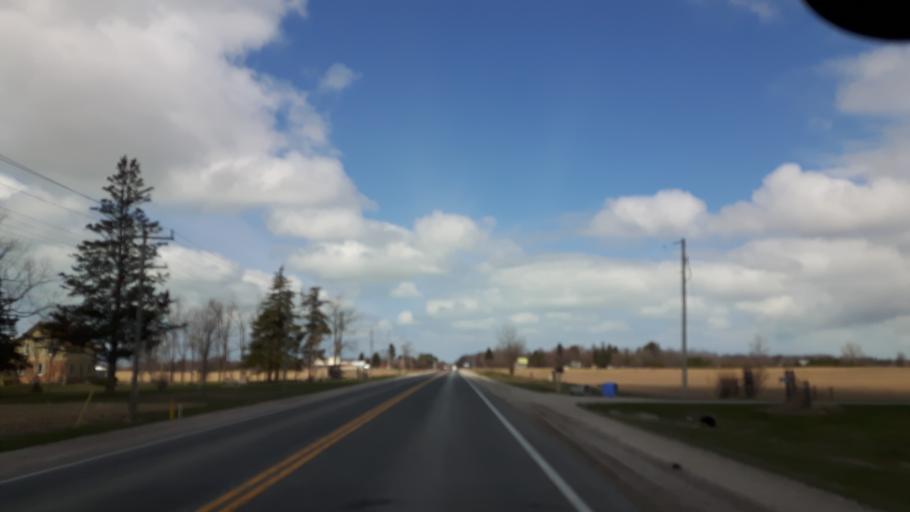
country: CA
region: Ontario
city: Goderich
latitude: 43.7198
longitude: -81.6739
